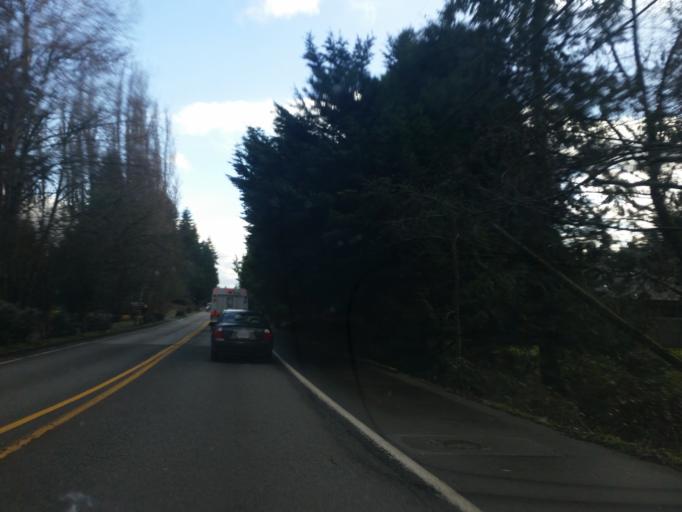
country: US
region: Washington
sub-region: Snohomish County
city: Mountlake Terrace
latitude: 47.7692
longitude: -122.3015
